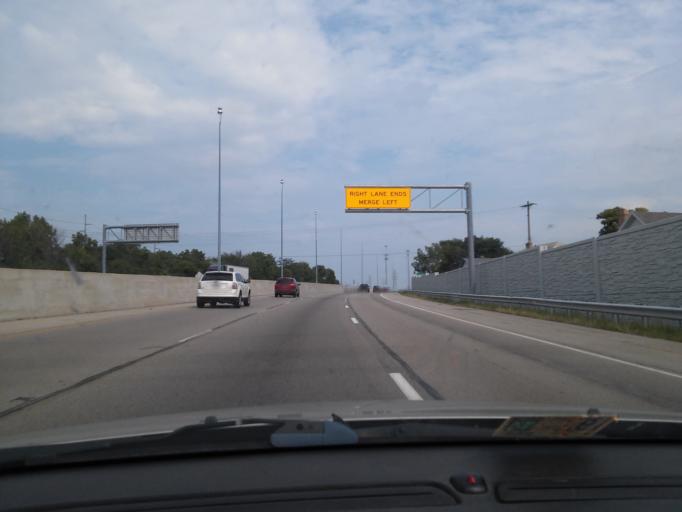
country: US
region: Ohio
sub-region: Montgomery County
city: Riverside
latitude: 39.7539
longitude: -84.1485
